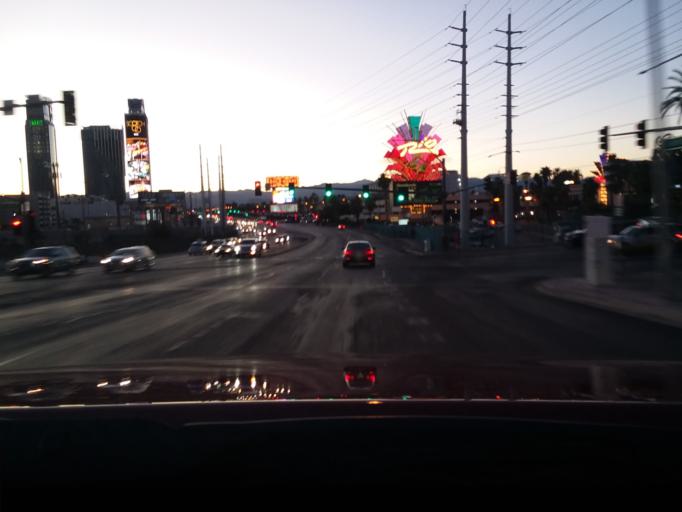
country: US
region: Nevada
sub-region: Clark County
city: Paradise
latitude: 36.1152
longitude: -115.1867
